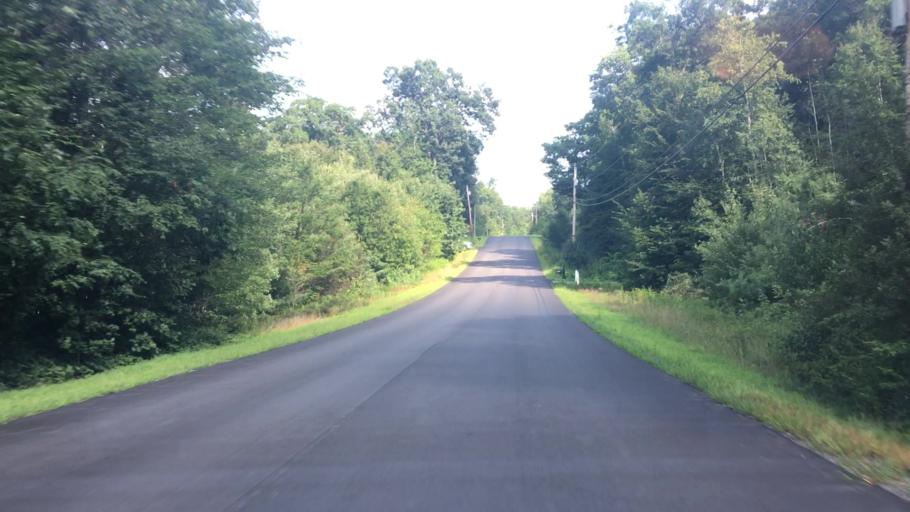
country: US
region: New Hampshire
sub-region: Rockingham County
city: Derry Village
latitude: 42.9388
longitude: -71.3303
